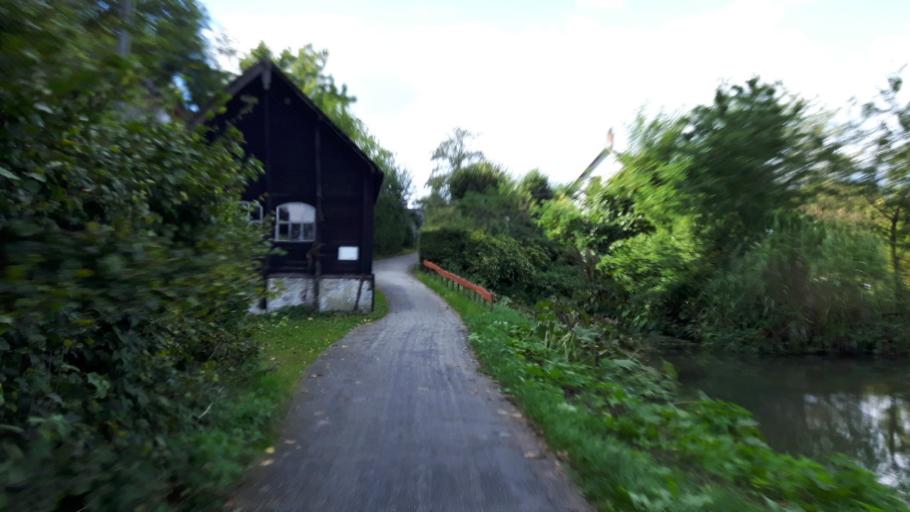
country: NL
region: South Holland
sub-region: Gemeente Leerdam
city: Leerdam
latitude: 51.8795
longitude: 5.0902
